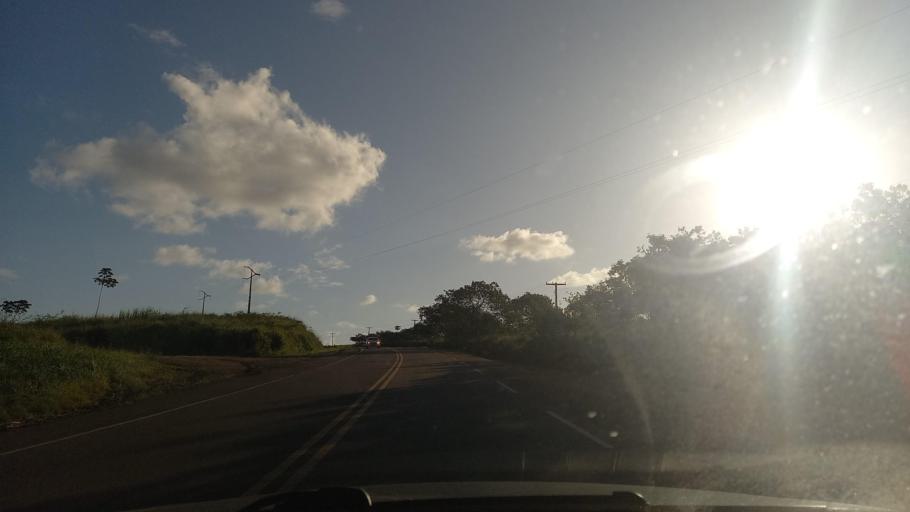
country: BR
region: Alagoas
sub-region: Sao Miguel Dos Campos
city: Sao Miguel dos Campos
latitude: -9.8045
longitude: -36.2044
